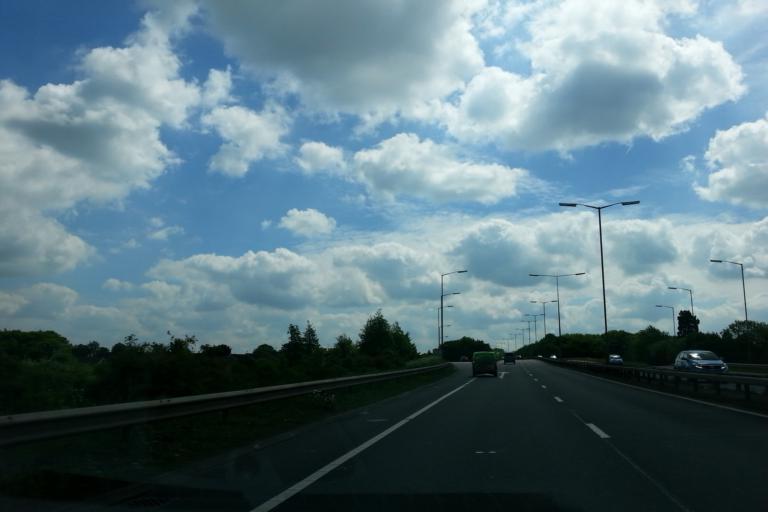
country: GB
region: England
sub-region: Peterborough
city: Peterborough
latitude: 52.5595
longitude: -0.2786
